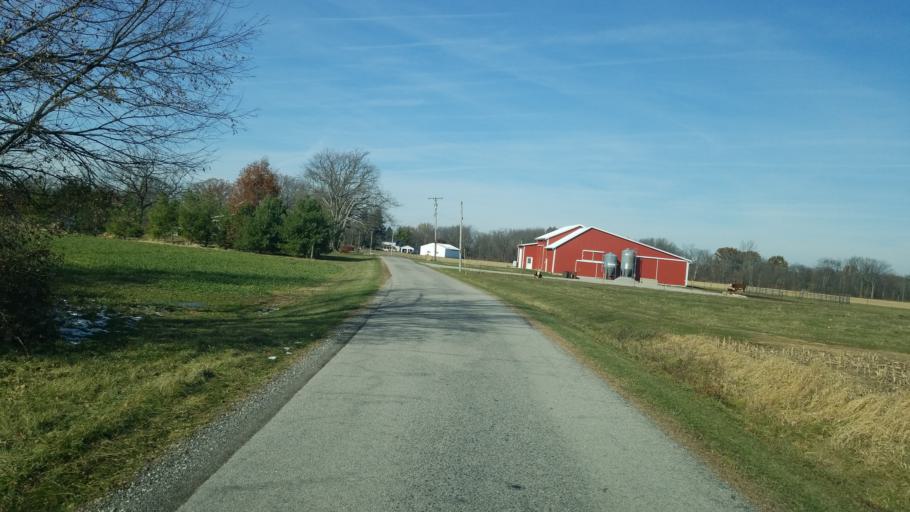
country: US
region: Ohio
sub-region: Huron County
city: Wakeman
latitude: 41.2178
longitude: -82.4128
